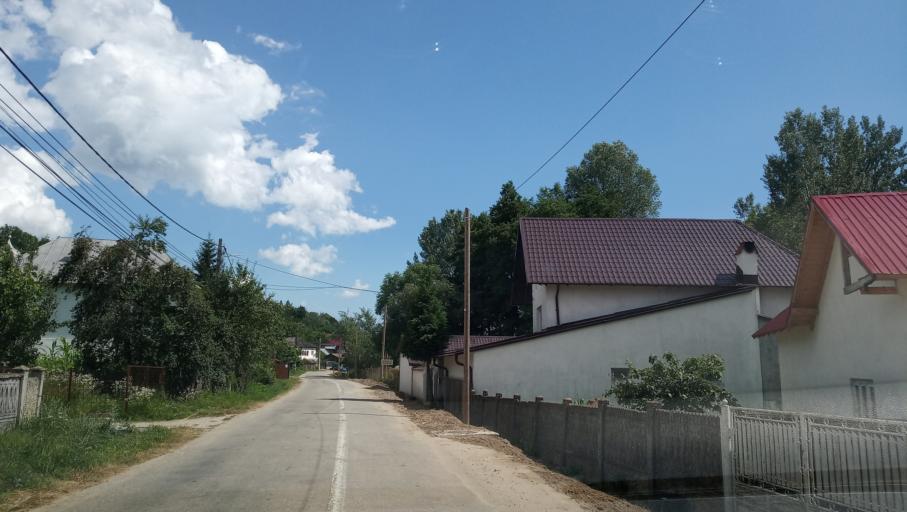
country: RO
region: Valcea
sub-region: Comuna Barbatesti
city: Bodesti
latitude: 45.1399
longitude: 24.1455
